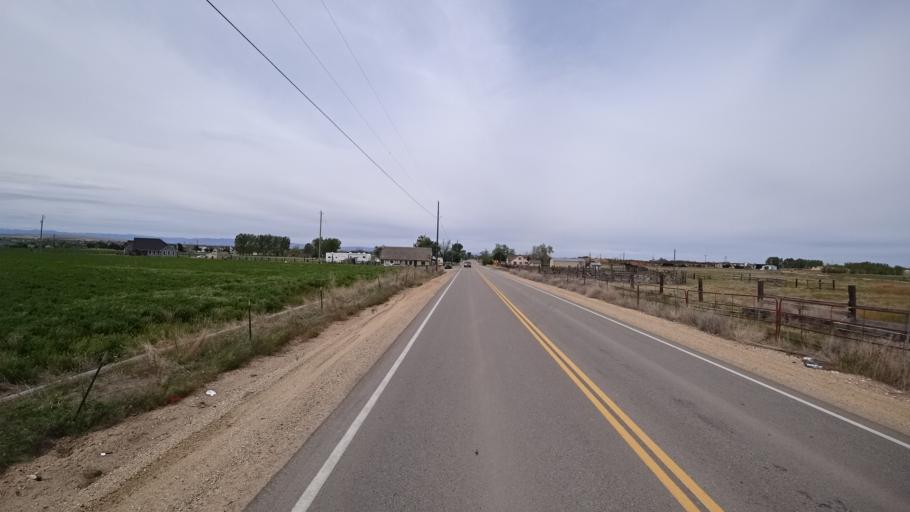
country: US
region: Idaho
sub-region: Ada County
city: Kuna
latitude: 43.5318
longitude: -116.3712
